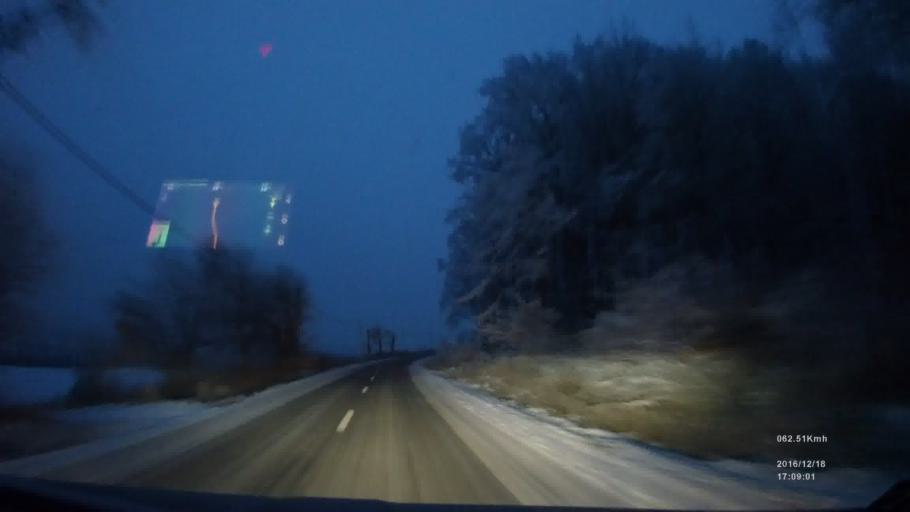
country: SK
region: Presovsky
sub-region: Okres Presov
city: Presov
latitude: 48.8785
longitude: 21.3113
